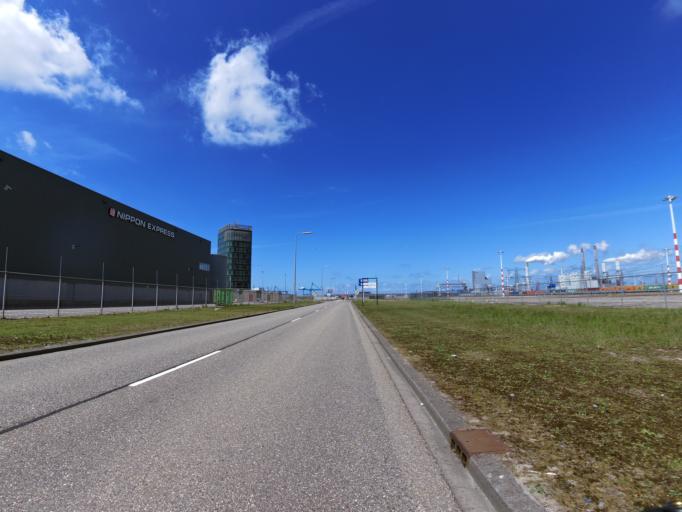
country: NL
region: South Holland
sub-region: Gemeente Rotterdam
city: Hoek van Holland
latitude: 51.9459
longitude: 4.0206
